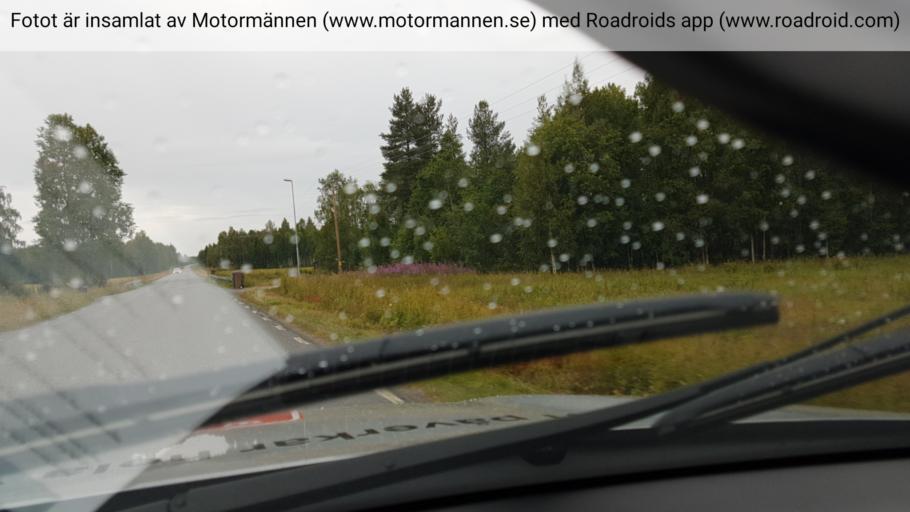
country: SE
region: Norrbotten
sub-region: Bodens Kommun
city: Boden
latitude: 65.8247
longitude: 21.5245
